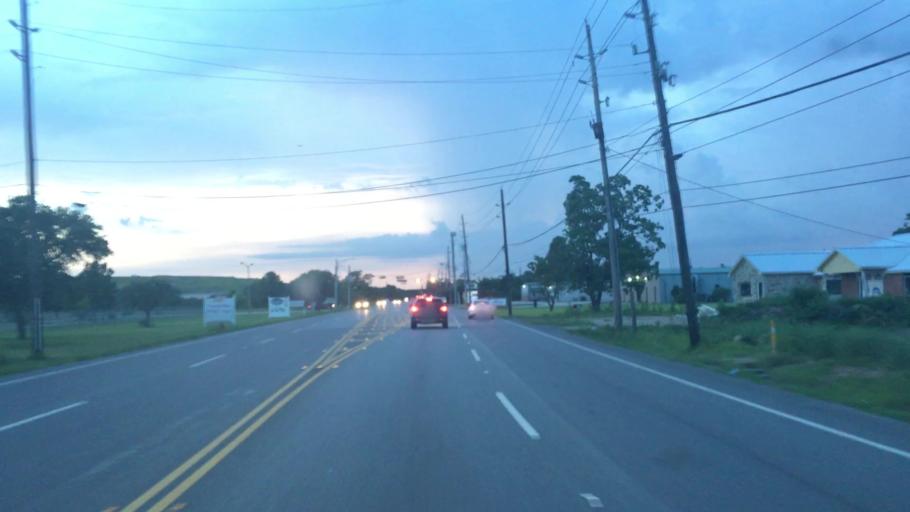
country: US
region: Texas
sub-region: Harris County
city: Humble
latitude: 29.9706
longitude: -95.2329
